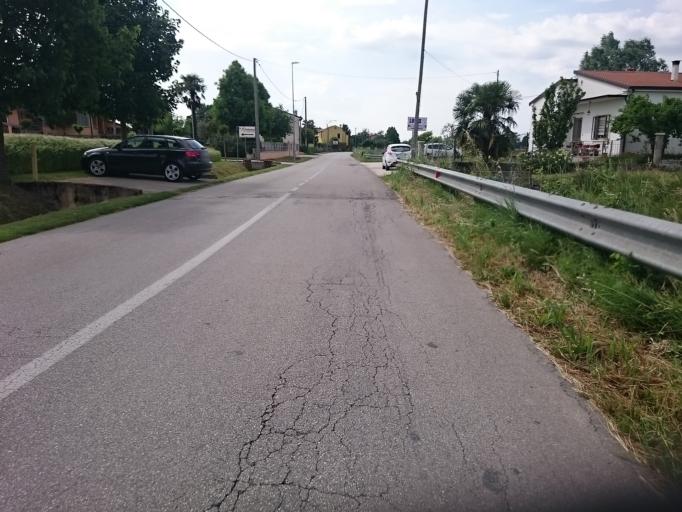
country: IT
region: Veneto
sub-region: Provincia di Padova
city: Megliadino San Vitale
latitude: 45.1939
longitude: 11.5206
